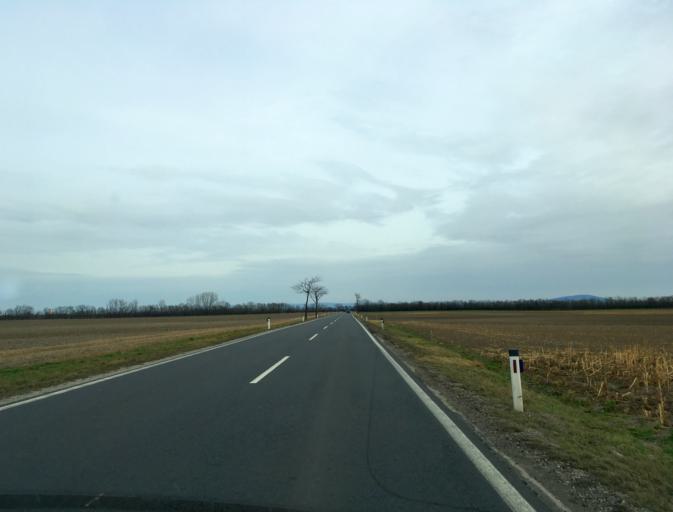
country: AT
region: Lower Austria
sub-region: Politischer Bezirk Ganserndorf
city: Untersiebenbrunn
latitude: 48.2217
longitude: 16.7528
